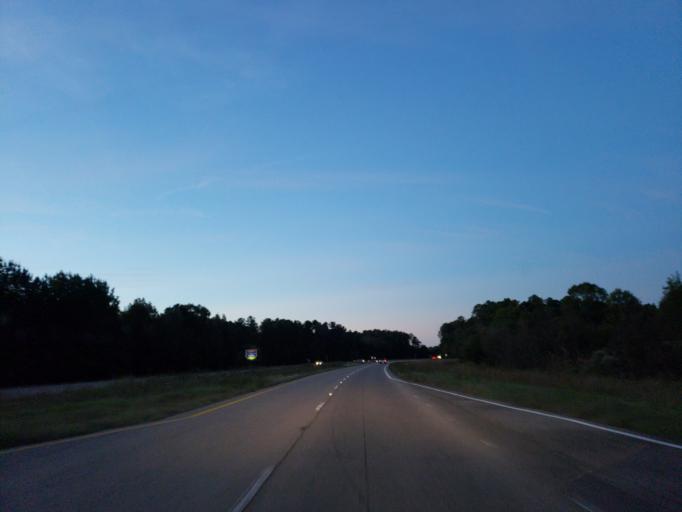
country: US
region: Mississippi
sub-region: Clarke County
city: Quitman
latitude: 31.8550
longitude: -88.7197
